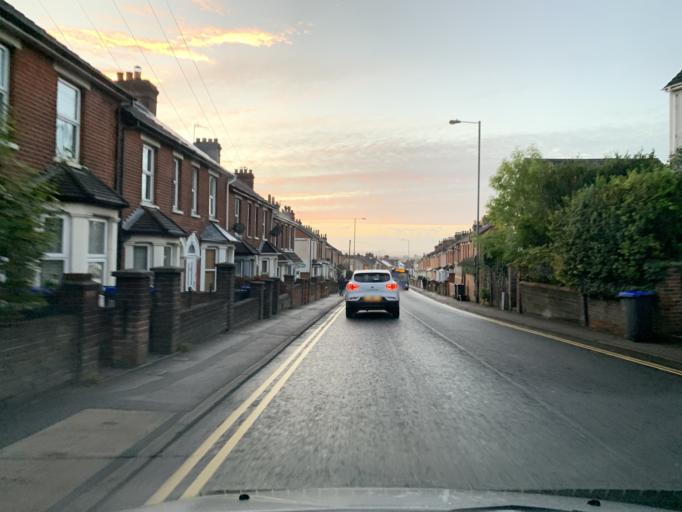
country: GB
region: England
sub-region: Wiltshire
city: Salisbury
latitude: 51.0768
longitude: -1.8106
